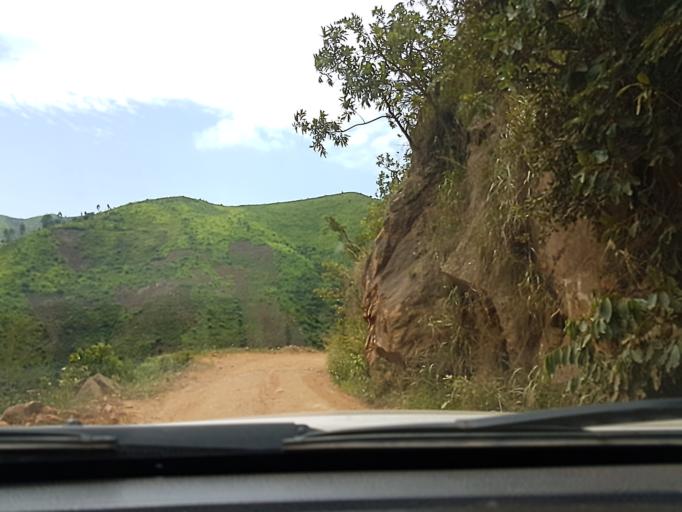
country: RW
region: Western Province
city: Cyangugu
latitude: -2.7061
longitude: 28.9450
